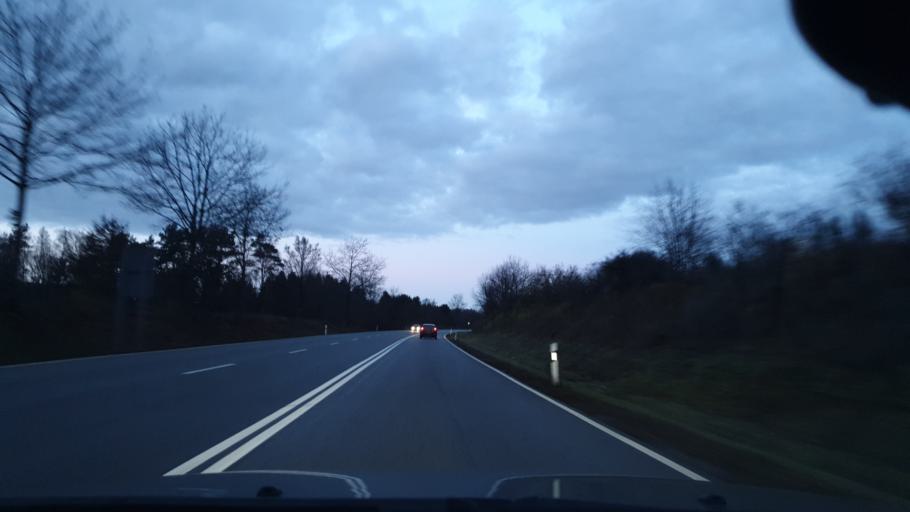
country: DE
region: Rheinland-Pfalz
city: Schopp
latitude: 49.3463
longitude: 7.6794
